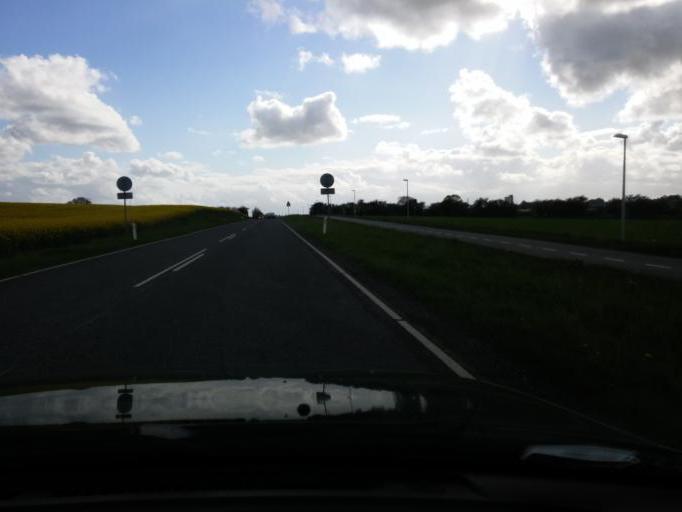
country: DK
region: South Denmark
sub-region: Faaborg-Midtfyn Kommune
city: Ringe
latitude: 55.2420
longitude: 10.5039
